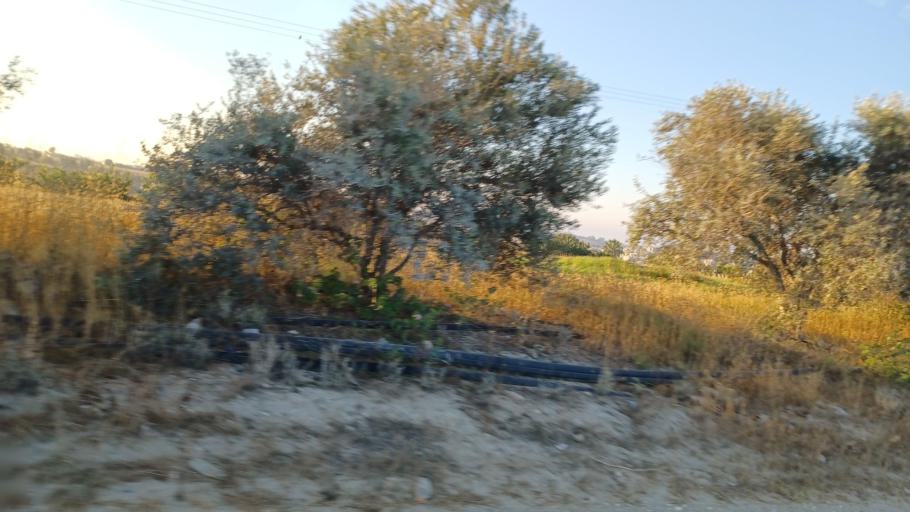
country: CY
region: Larnaka
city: Xylotymbou
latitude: 34.9988
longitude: 33.7749
